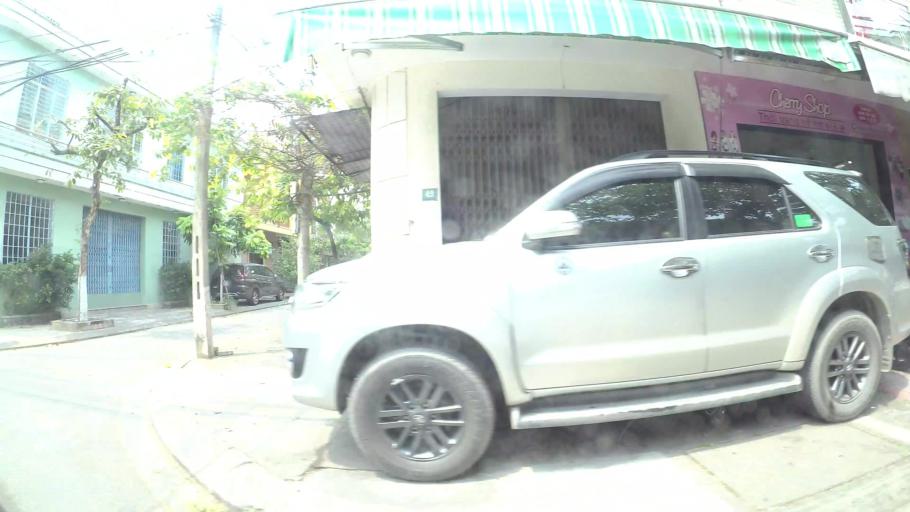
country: VN
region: Da Nang
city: Da Nang
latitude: 16.0885
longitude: 108.2170
